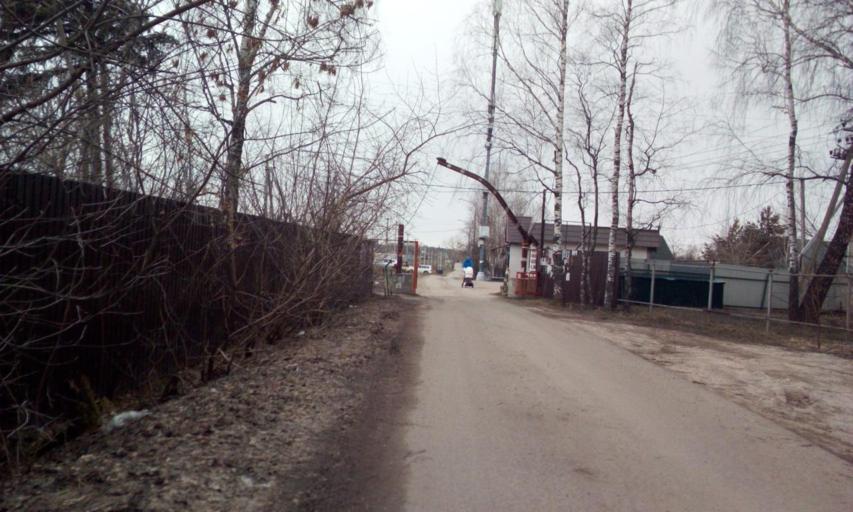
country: RU
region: Moskovskaya
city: Kommunarka
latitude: 55.5230
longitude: 37.4925
